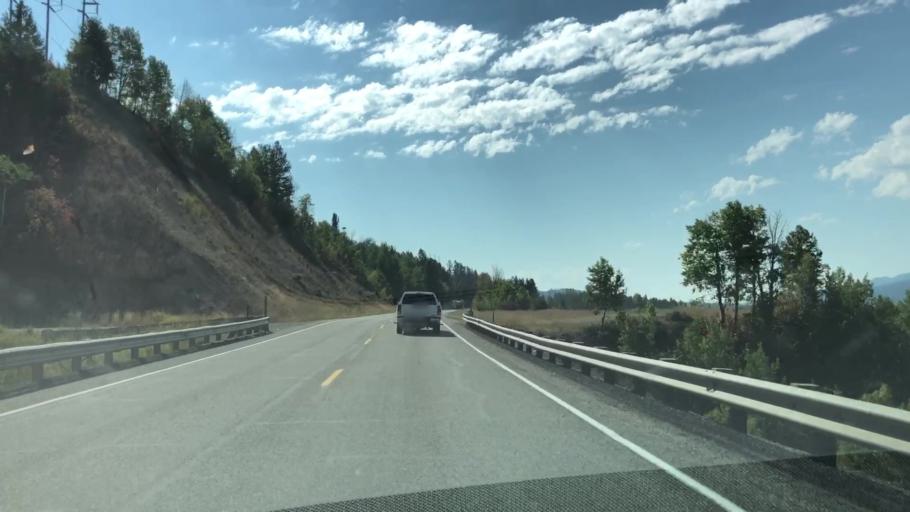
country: US
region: Idaho
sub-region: Teton County
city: Victor
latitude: 43.2936
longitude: -111.1255
